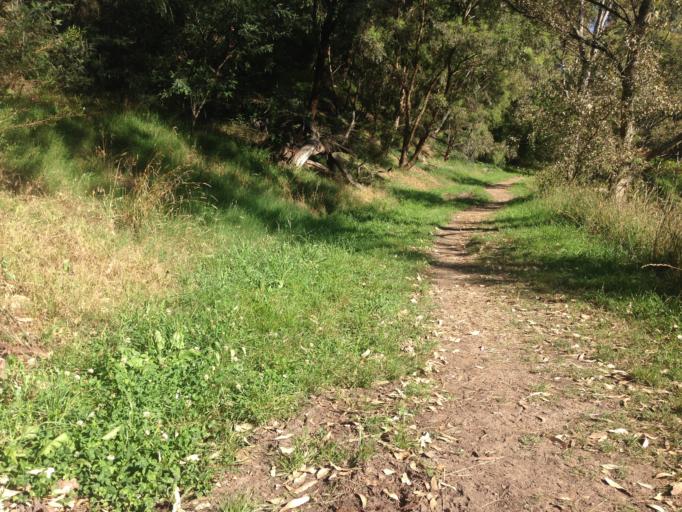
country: AU
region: Victoria
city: Heidelberg West
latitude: -37.7595
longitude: 145.0298
